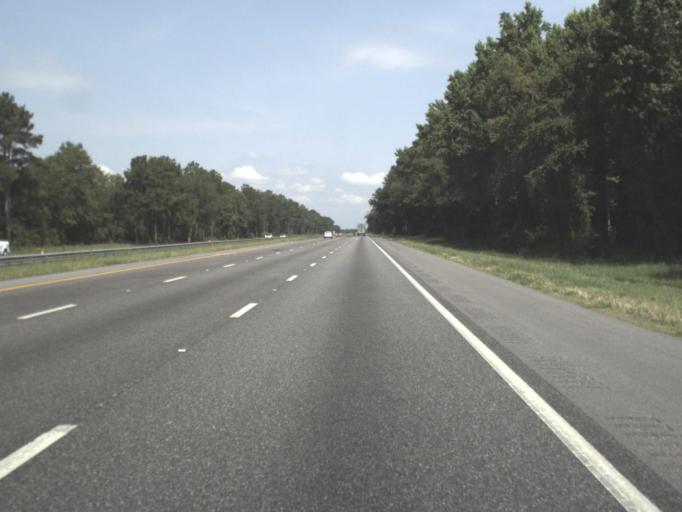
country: US
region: Florida
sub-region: Hamilton County
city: Jasper
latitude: 30.4666
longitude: -82.9621
